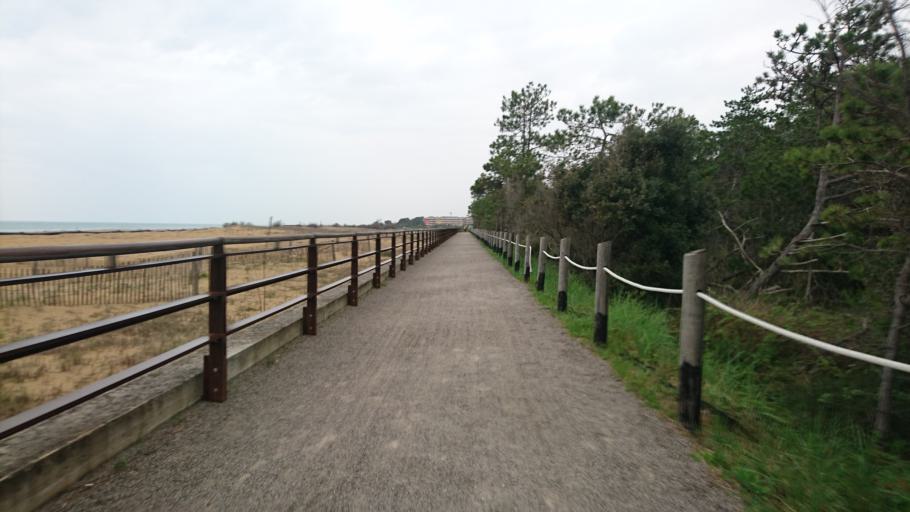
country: IT
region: Veneto
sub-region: Provincia di Venezia
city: Bibione
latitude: 45.6357
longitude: 13.0826
